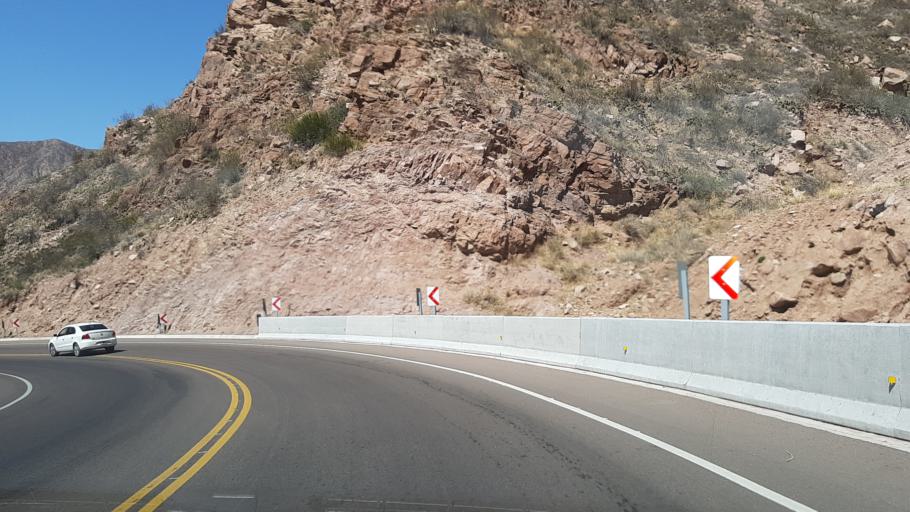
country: AR
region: Mendoza
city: Lujan de Cuyo
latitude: -33.0029
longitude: -69.1319
